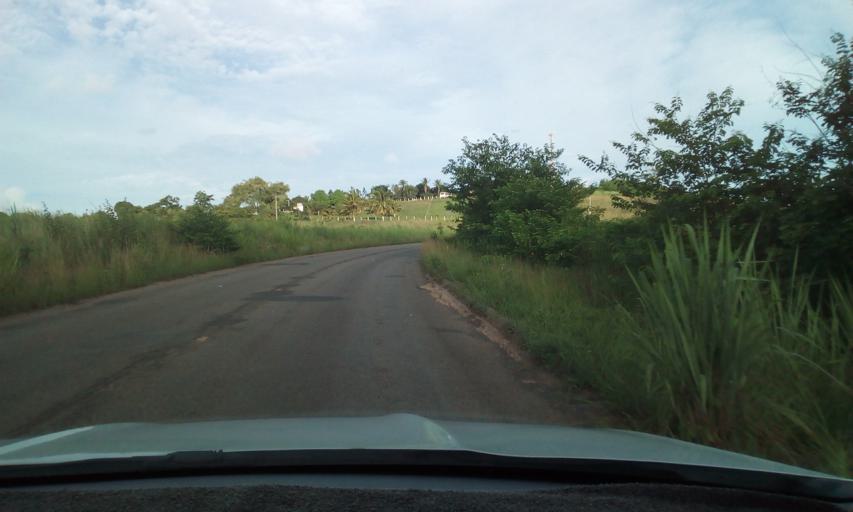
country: BR
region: Pernambuco
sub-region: Gloria Do Goita
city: Gloria do Goita
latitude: -7.9953
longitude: -35.2261
